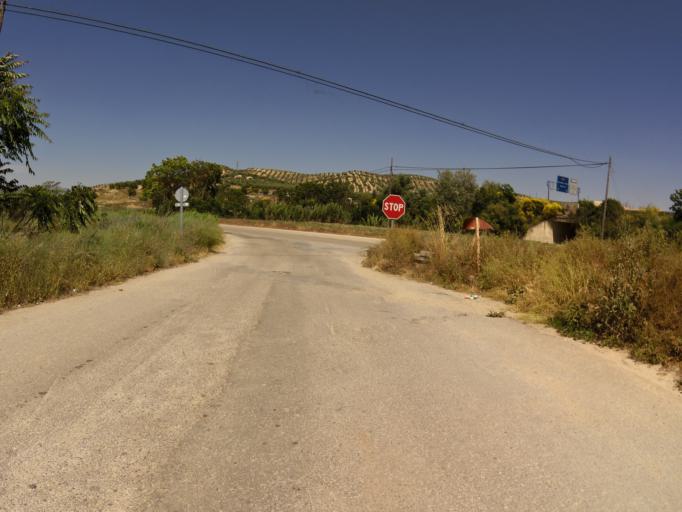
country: ES
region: Andalusia
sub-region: Provincia de Granada
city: Salar
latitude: 37.1677
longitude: -4.0885
